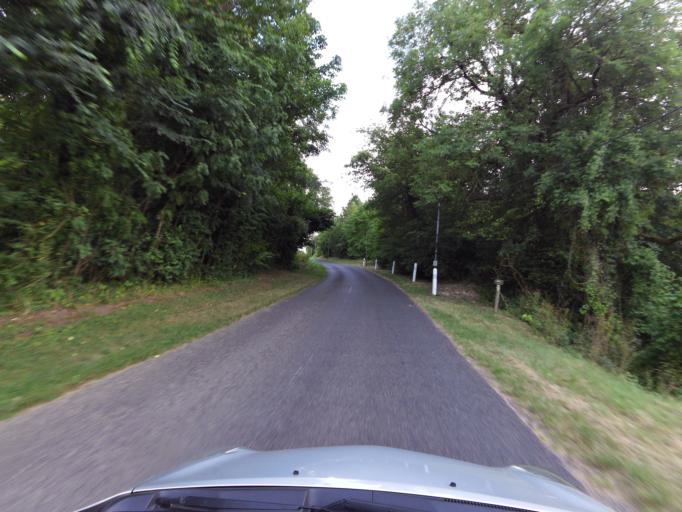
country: FR
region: Picardie
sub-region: Departement de l'Aisne
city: Bruyeres-et-Montberault
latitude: 49.5028
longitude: 3.6278
